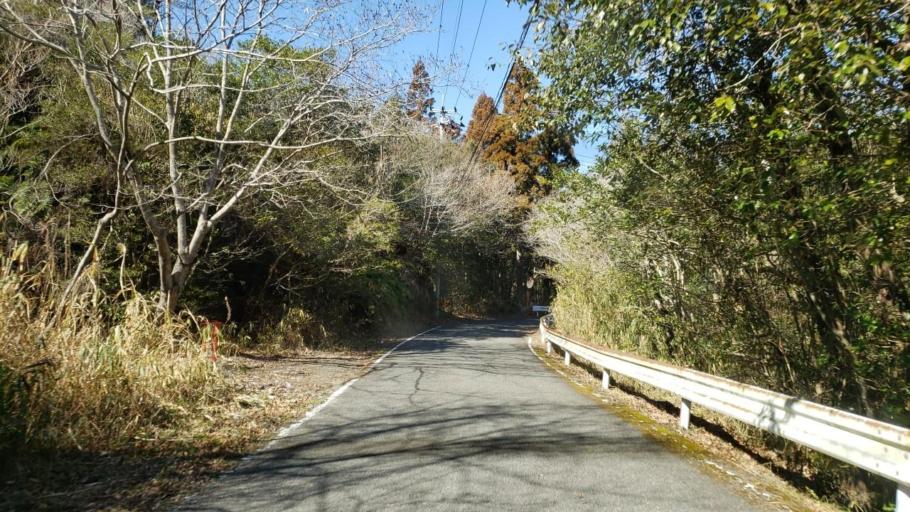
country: JP
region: Tokushima
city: Narutocho-mitsuishi
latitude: 34.1917
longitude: 134.5524
